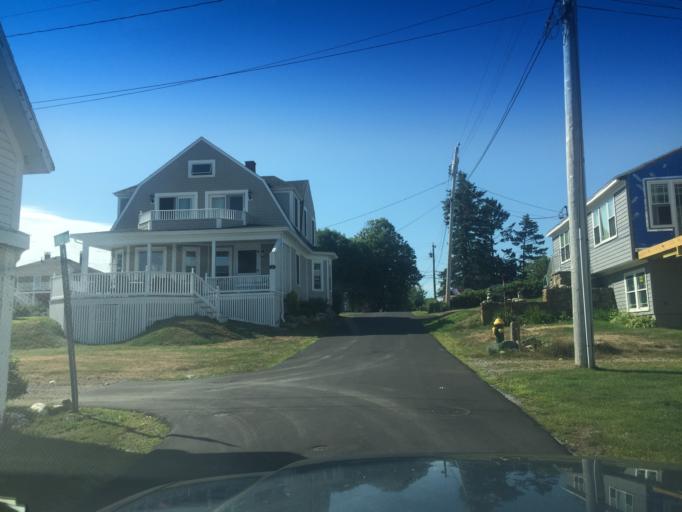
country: US
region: Maine
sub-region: York County
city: York Beach
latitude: 43.1732
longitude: -70.6039
